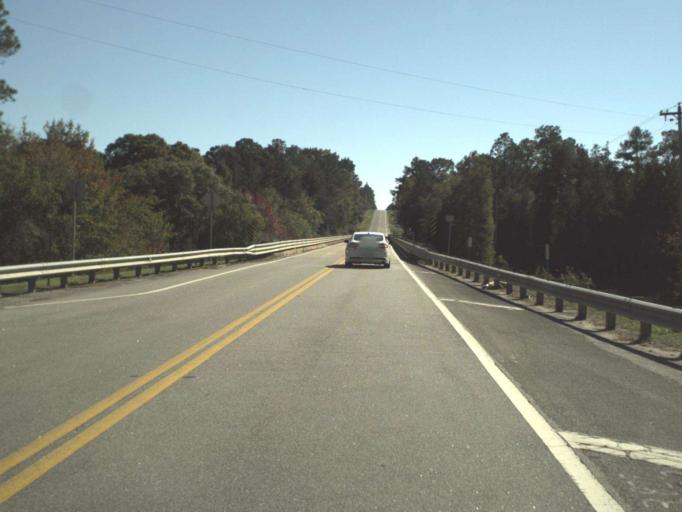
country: US
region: Florida
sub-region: Okaloosa County
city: Crestview
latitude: 30.8342
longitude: -86.7346
